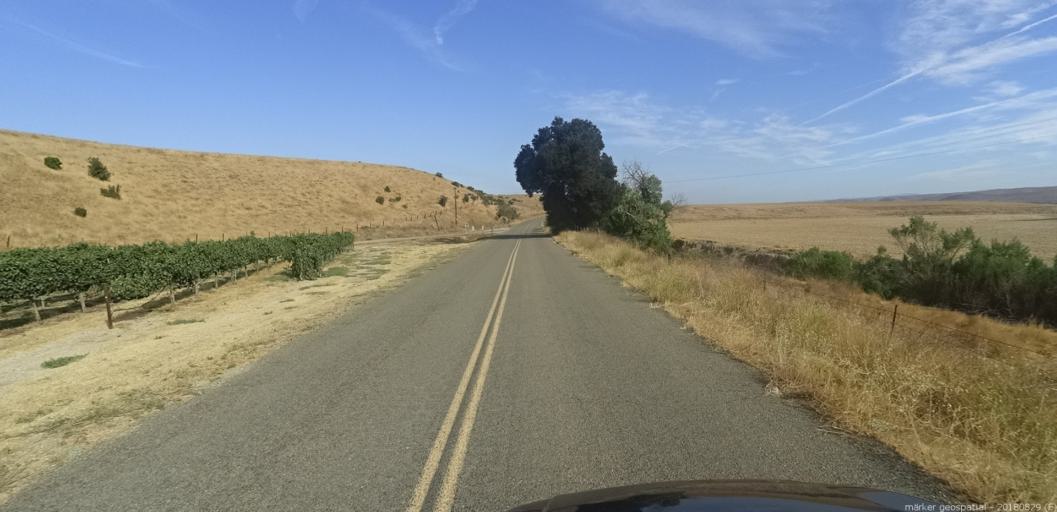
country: US
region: California
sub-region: Monterey County
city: King City
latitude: 36.0851
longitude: -121.0062
